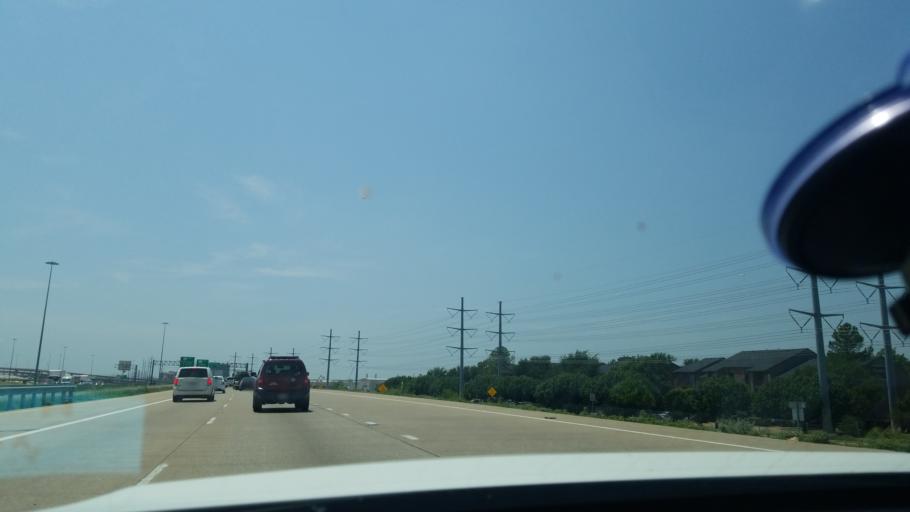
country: US
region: Texas
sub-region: Tarrant County
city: Euless
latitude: 32.8539
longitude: -97.0160
